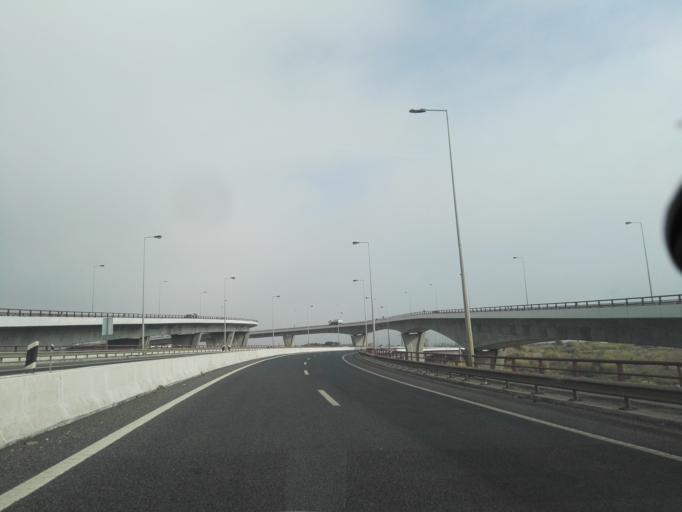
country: PT
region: Lisbon
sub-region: Loures
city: Sacavem
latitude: 38.7963
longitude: -9.0987
